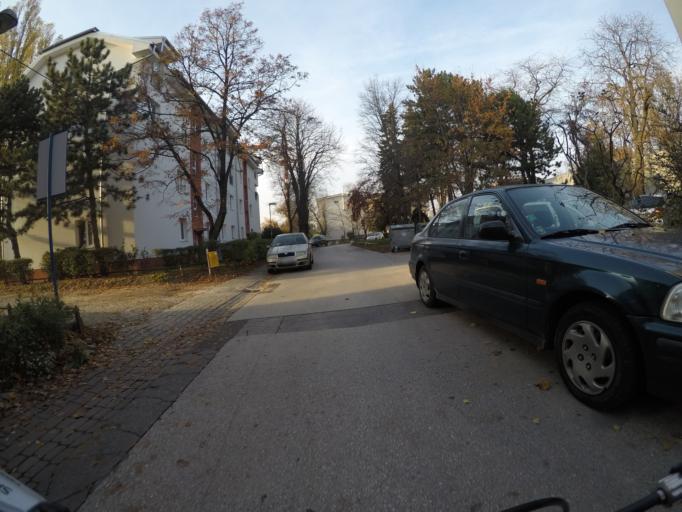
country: SK
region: Bratislavsky
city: Bratislava
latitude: 48.1750
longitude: 17.1573
